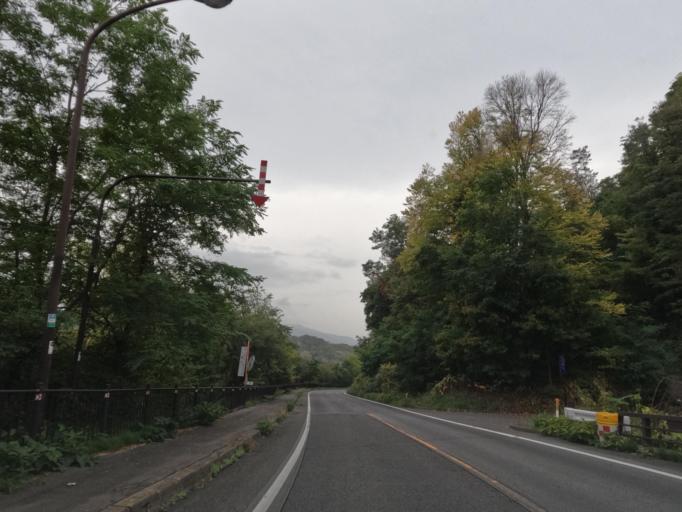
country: JP
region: Hokkaido
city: Date
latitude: 42.5265
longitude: 140.8616
